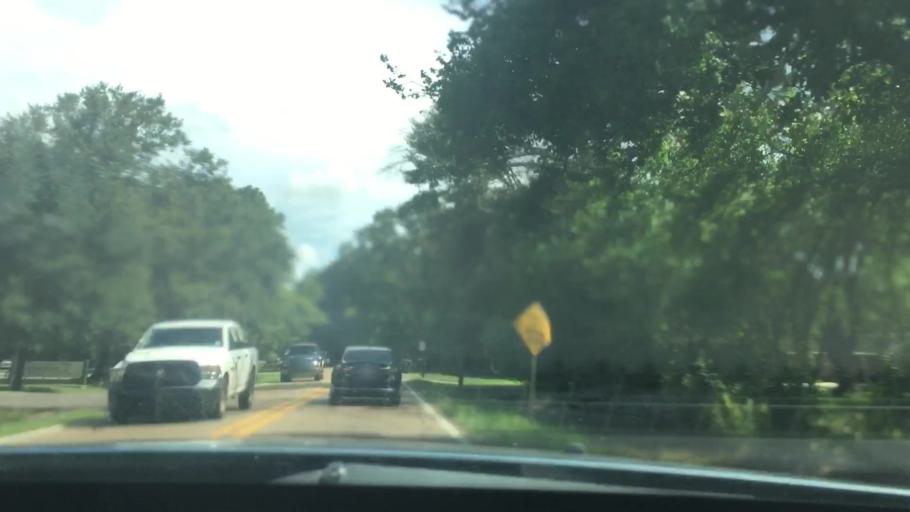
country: US
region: Louisiana
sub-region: East Baton Rouge Parish
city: Westminster
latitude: 30.4506
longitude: -91.0708
